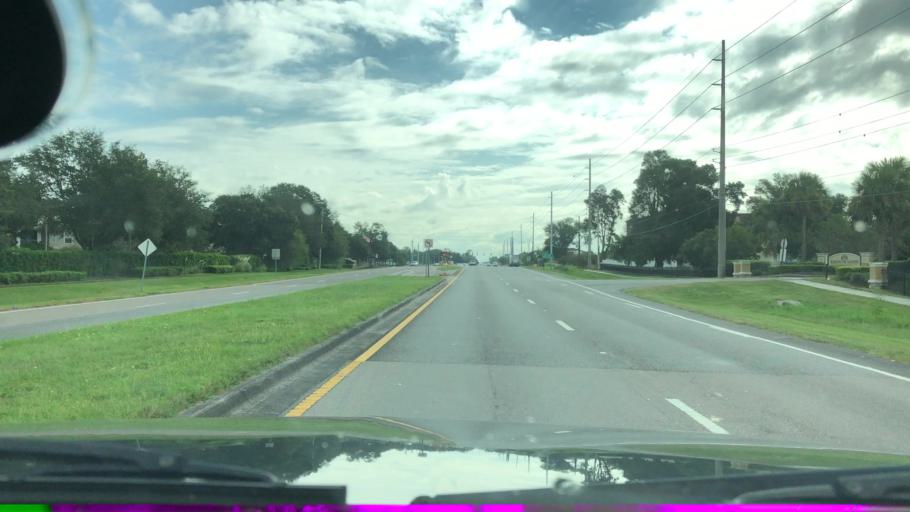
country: US
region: Florida
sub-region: Hillsborough County
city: Progress Village
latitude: 27.8938
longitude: -82.3423
